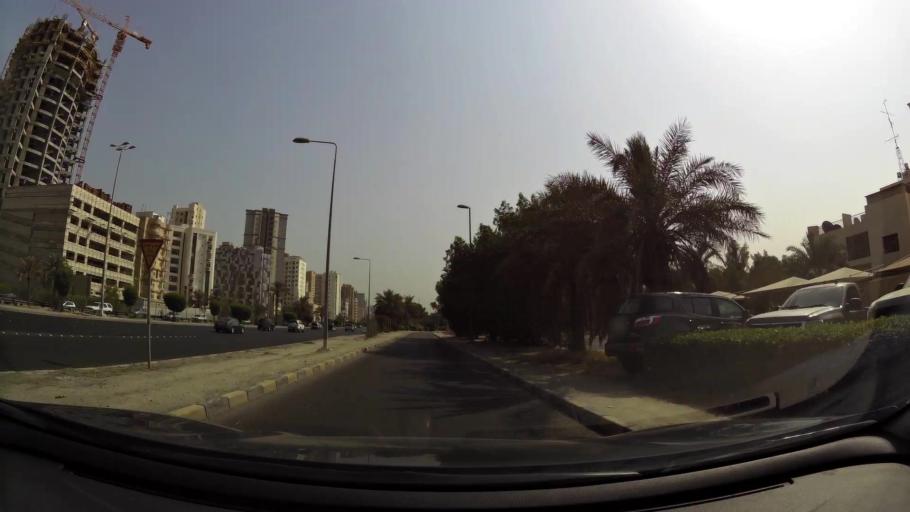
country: KW
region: Muhafazat Hawalli
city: Hawalli
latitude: 29.3553
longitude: 48.0229
